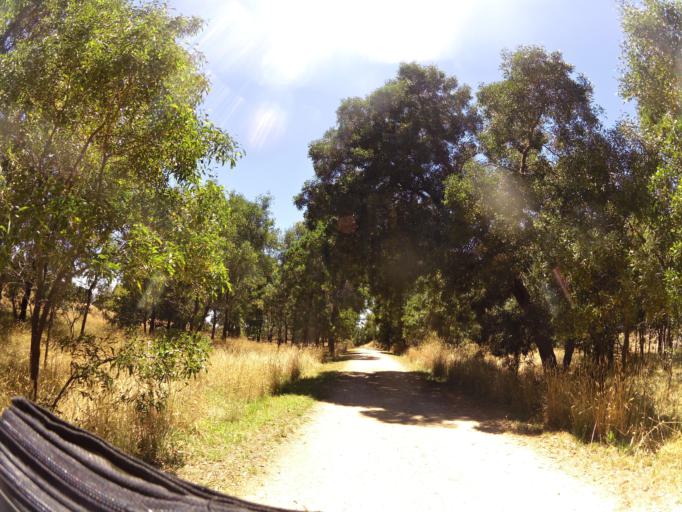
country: AU
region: Victoria
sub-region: Ballarat North
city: Delacombe
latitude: -37.6149
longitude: 143.7115
